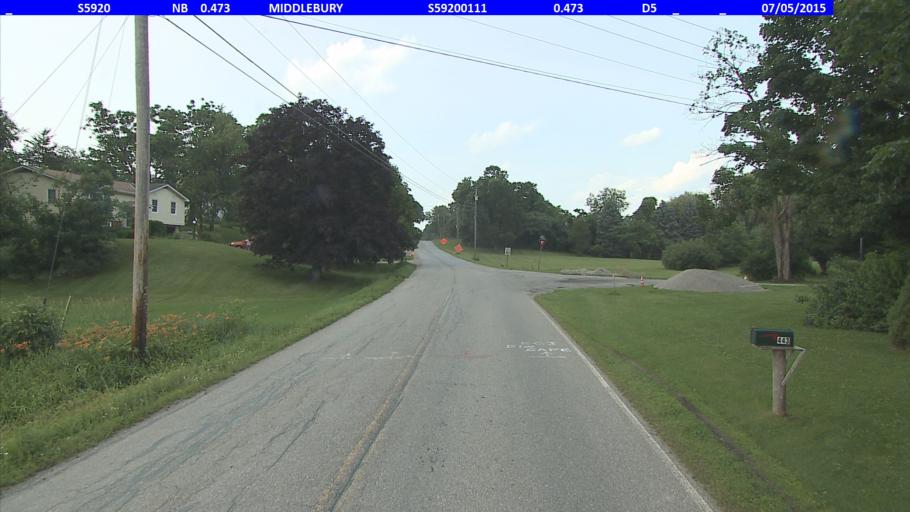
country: US
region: Vermont
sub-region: Addison County
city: Middlebury (village)
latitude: 43.9950
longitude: -73.1343
